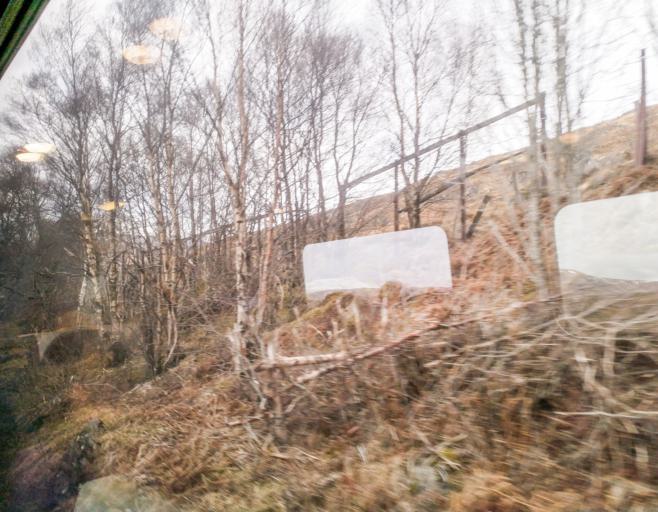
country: GB
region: Scotland
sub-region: Highland
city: Spean Bridge
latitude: 56.7752
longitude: -4.7278
